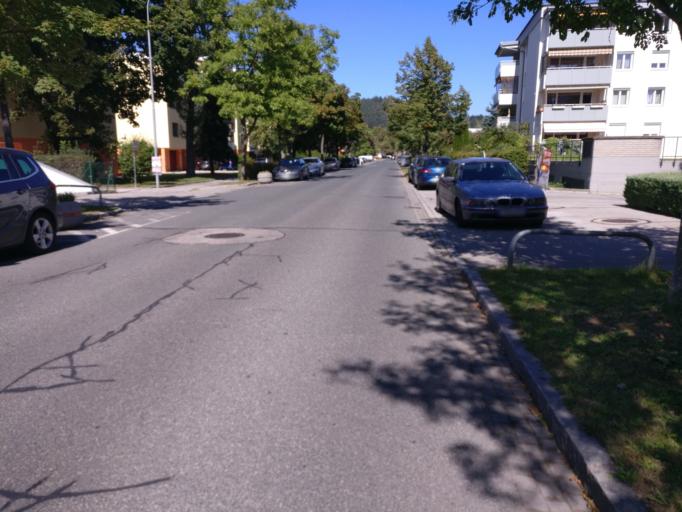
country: AT
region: Carinthia
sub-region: Klagenfurt am Woerthersee
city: Klagenfurt am Woerthersee
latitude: 46.6161
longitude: 14.2782
